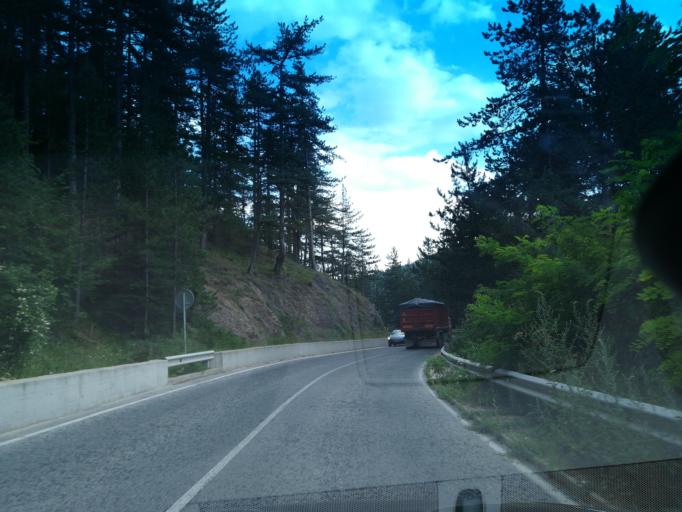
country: BG
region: Smolyan
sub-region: Obshtina Chepelare
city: Chepelare
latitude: 41.6637
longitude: 24.7517
